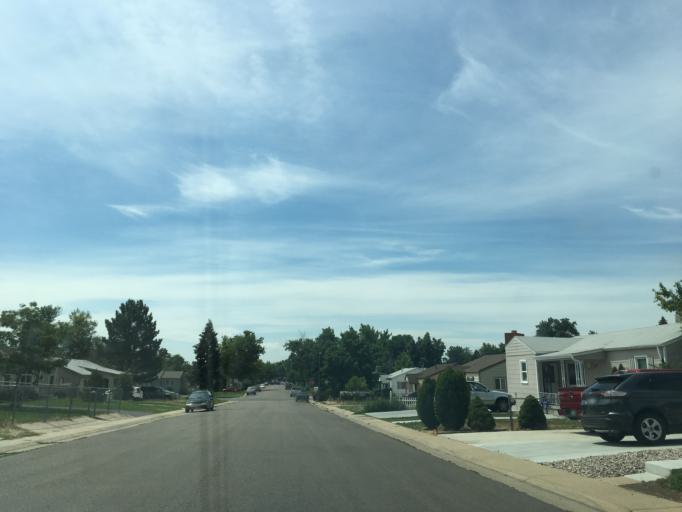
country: US
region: Colorado
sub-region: Jefferson County
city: Lakewood
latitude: 39.6922
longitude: -105.0367
